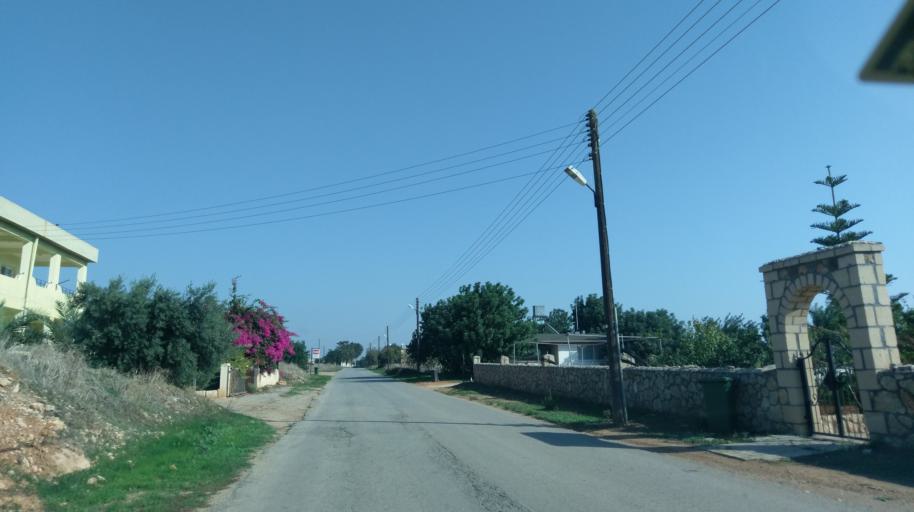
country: CY
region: Ammochostos
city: Leonarisso
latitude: 35.4810
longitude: 34.1782
